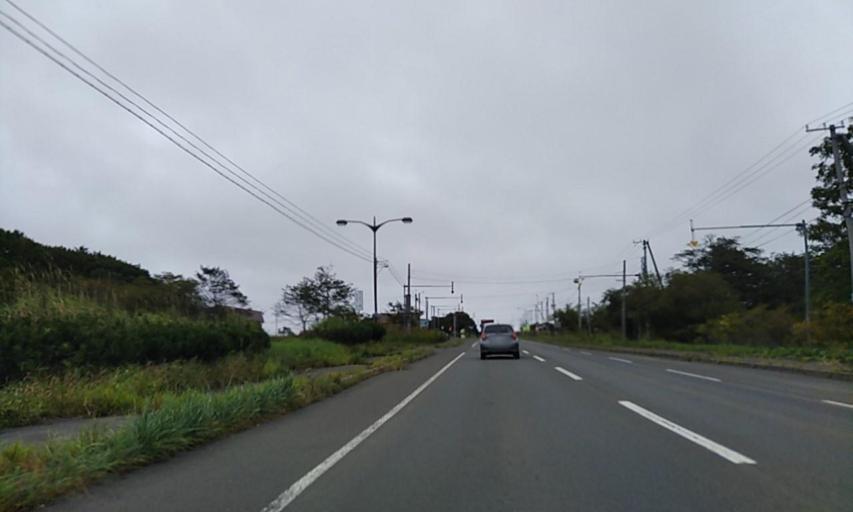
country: JP
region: Hokkaido
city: Nemuro
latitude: 43.2694
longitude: 145.4770
